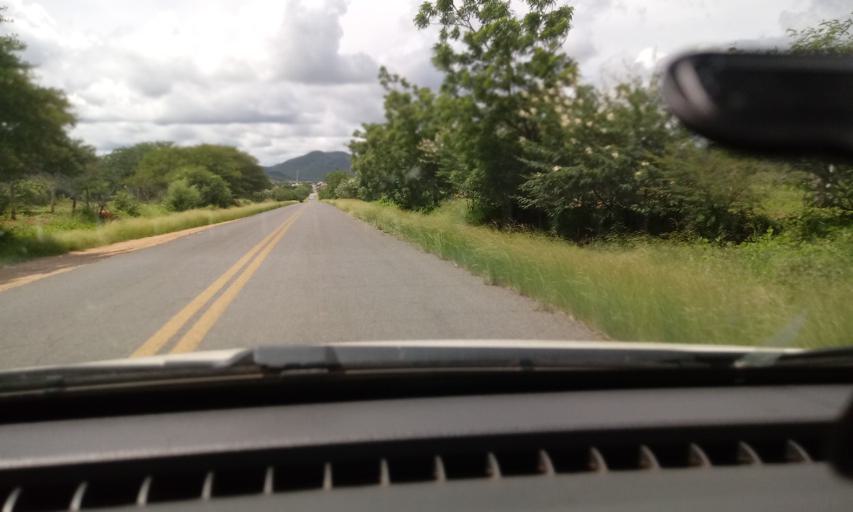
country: BR
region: Bahia
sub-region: Guanambi
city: Guanambi
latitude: -13.9254
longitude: -42.8468
